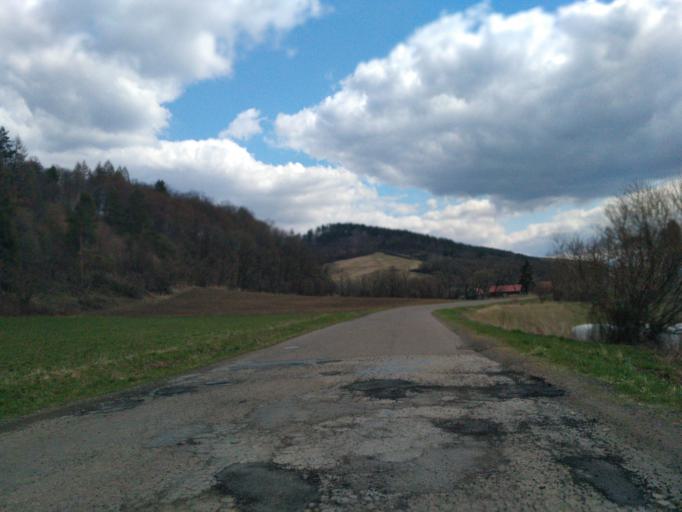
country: PL
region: Subcarpathian Voivodeship
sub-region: Powiat sanocki
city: Tyrawa Woloska
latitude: 49.6045
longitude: 22.3071
